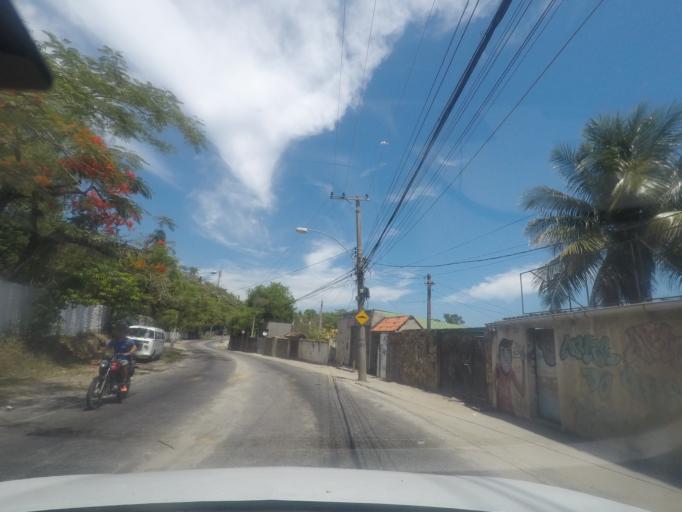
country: BR
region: Rio de Janeiro
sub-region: Itaguai
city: Itaguai
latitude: -22.9999
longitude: -43.6481
